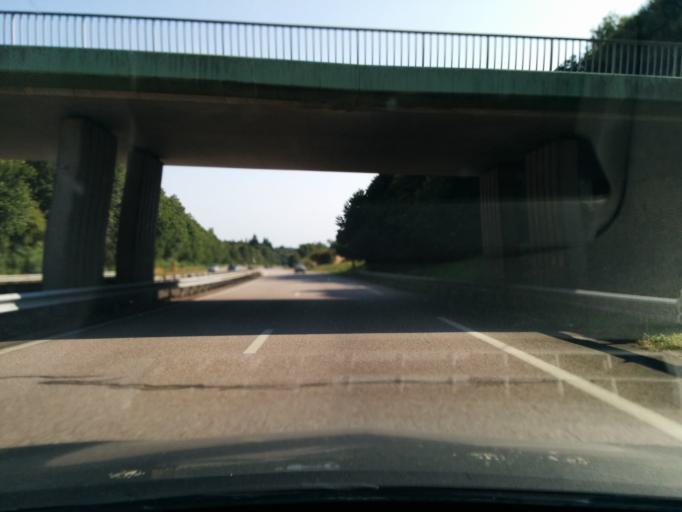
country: FR
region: Limousin
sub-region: Departement de la Haute-Vienne
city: Bonnac-la-Cote
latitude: 45.9386
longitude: 1.3047
